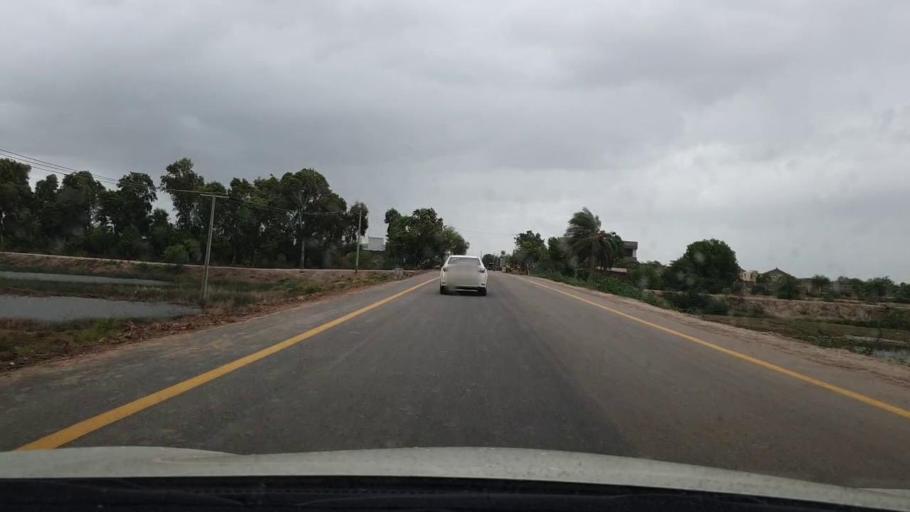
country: PK
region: Sindh
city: Badin
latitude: 24.6551
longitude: 68.8141
